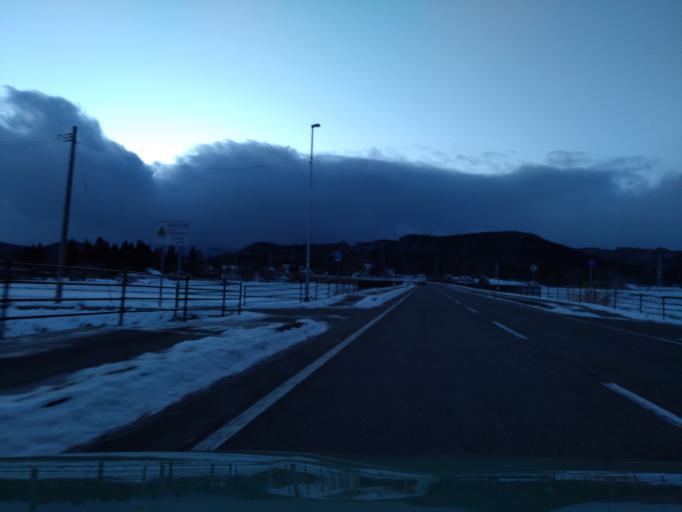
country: JP
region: Iwate
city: Shizukuishi
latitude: 39.6975
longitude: 140.9419
